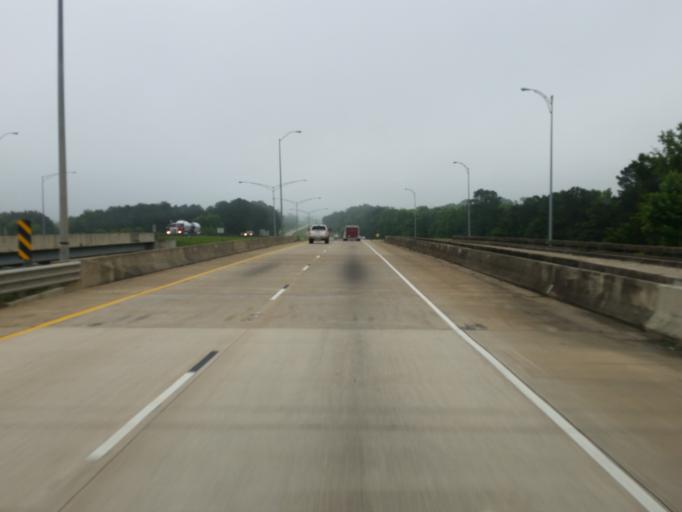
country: US
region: Louisiana
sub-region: Webster Parish
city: Minden
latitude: 32.5892
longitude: -93.2922
